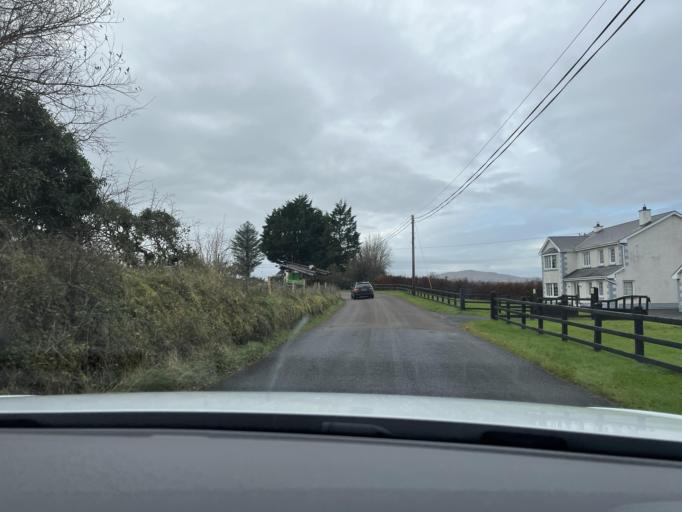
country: IE
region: Connaught
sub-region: County Leitrim
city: Manorhamilton
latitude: 54.2358
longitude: -8.2810
